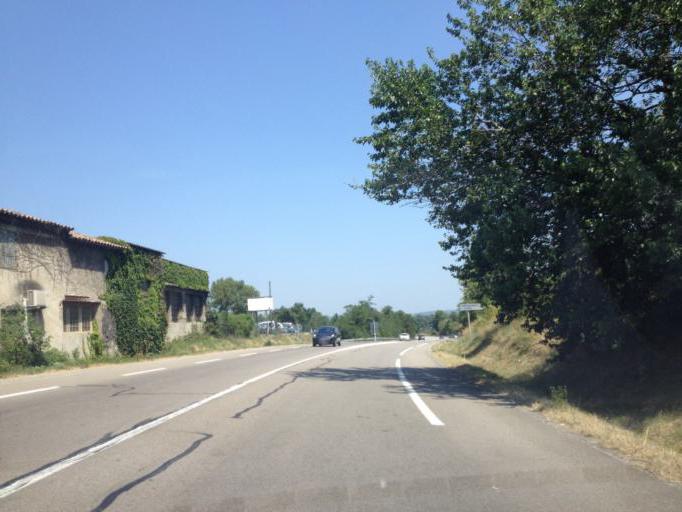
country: FR
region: Rhone-Alpes
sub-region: Departement de l'Ardeche
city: Cornas
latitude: 44.9876
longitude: 4.8797
